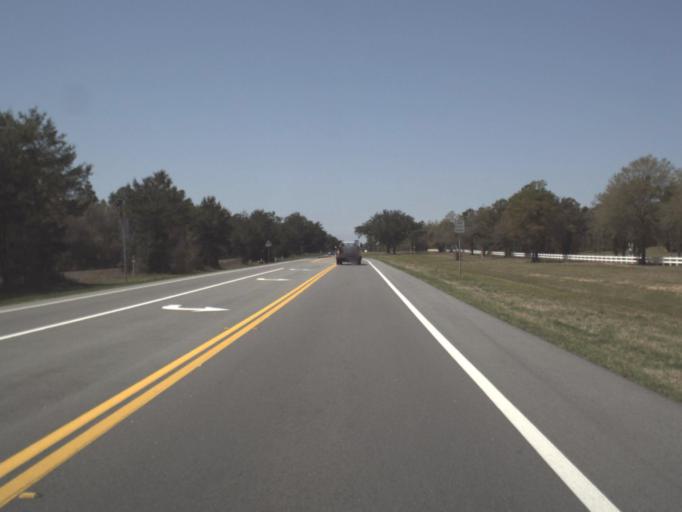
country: US
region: Florida
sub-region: Walton County
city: DeFuniak Springs
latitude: 30.7398
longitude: -86.3332
